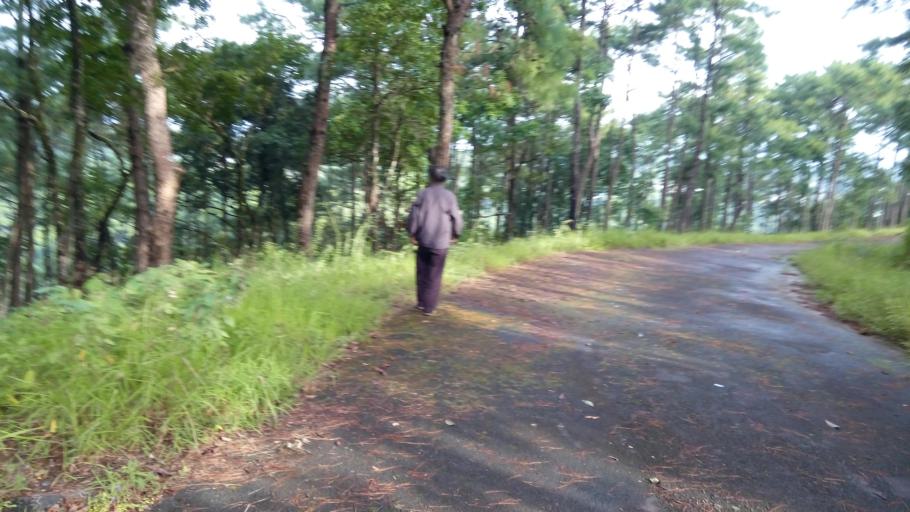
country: IN
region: Meghalaya
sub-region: East Khasi Hills
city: Shillong
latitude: 25.6070
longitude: 91.8793
